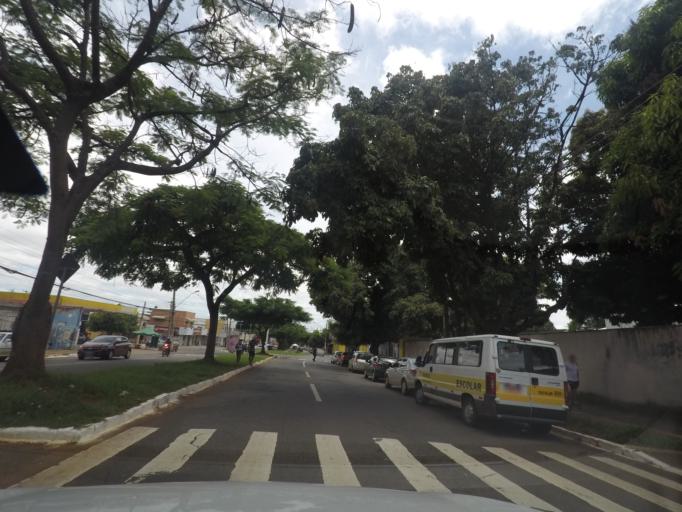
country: BR
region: Goias
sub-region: Goiania
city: Goiania
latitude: -16.6686
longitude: -49.2442
